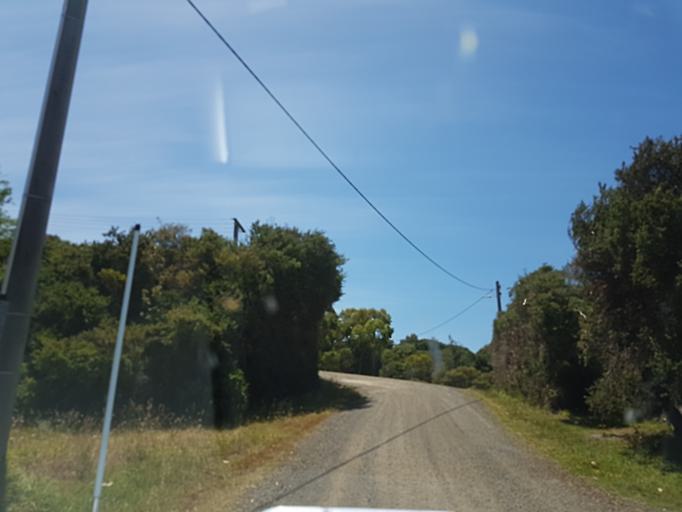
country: AU
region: Victoria
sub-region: Bass Coast
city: North Wonthaggi
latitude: -38.7018
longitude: 145.8285
